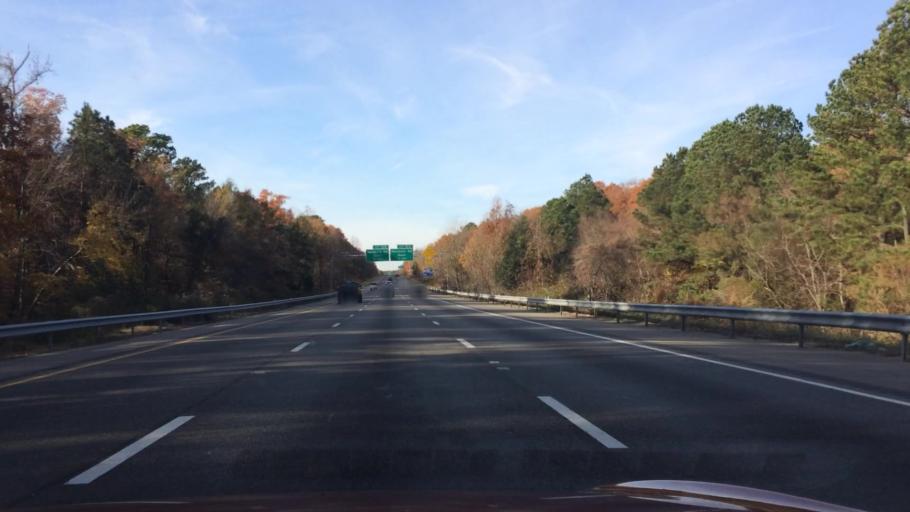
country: US
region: Virginia
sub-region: Henrico County
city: Wyndham
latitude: 37.6758
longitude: -77.5663
